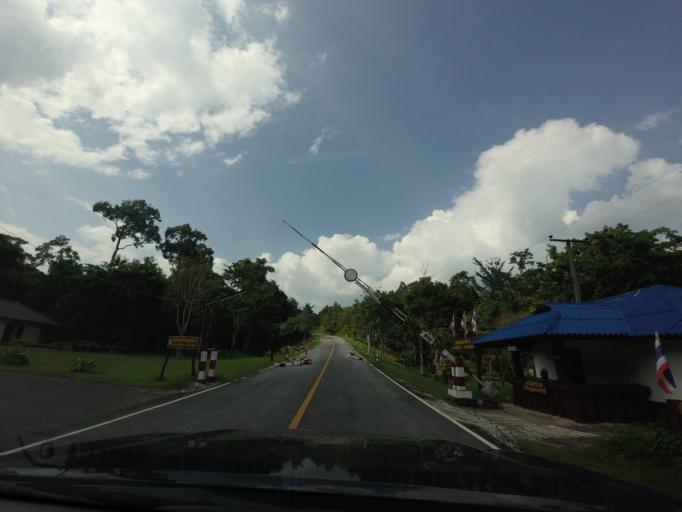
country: TH
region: Uttaradit
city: Ban Khok
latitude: 18.2149
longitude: 101.0367
